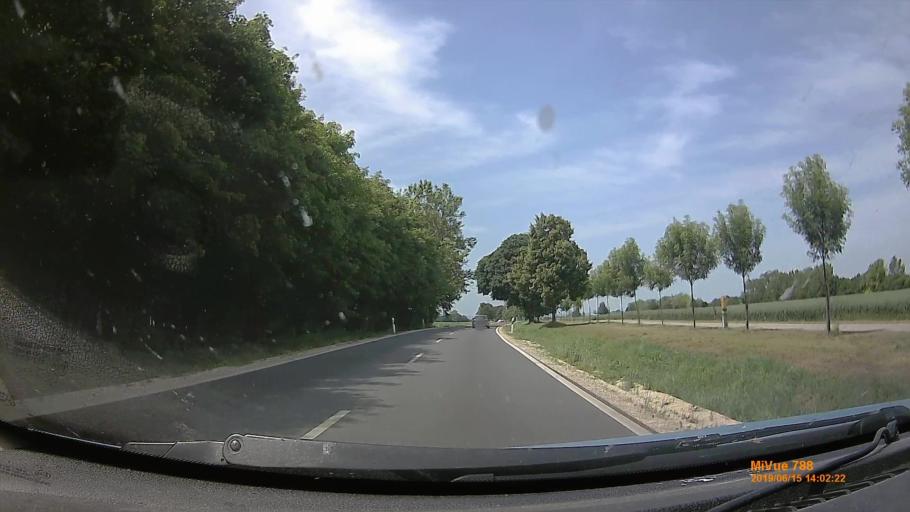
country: HU
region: Somogy
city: Siofok
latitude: 46.8585
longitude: 18.0889
